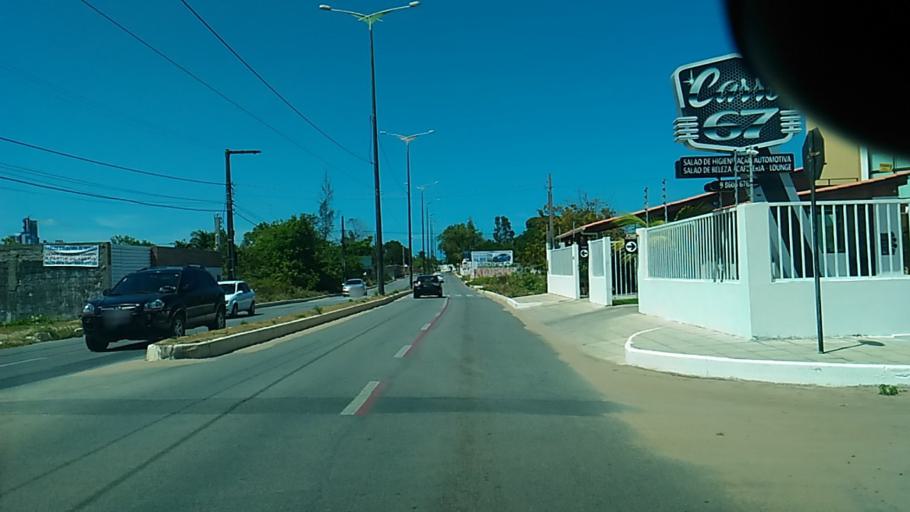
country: BR
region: Paraiba
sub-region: Joao Pessoa
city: Joao Pessoa
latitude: -7.1470
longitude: -34.8170
